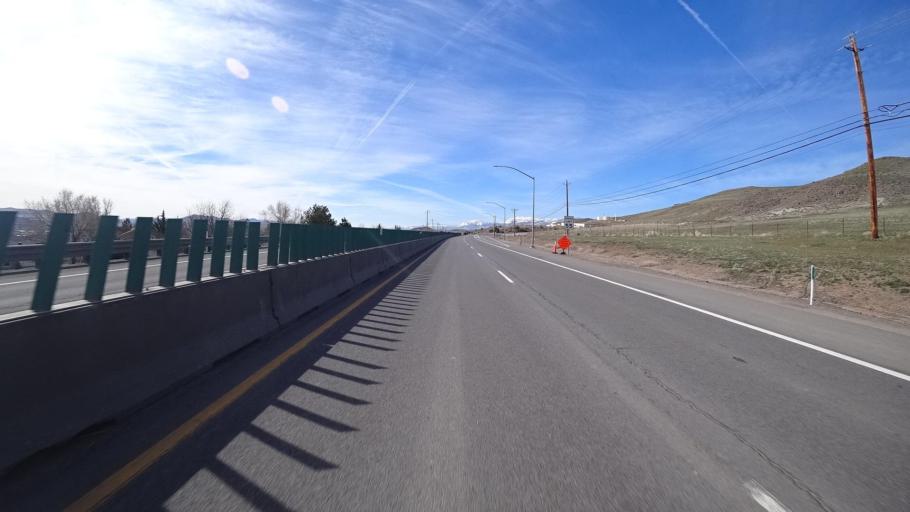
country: US
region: Nevada
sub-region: Washoe County
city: Sun Valley
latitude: 39.5984
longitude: -119.7367
